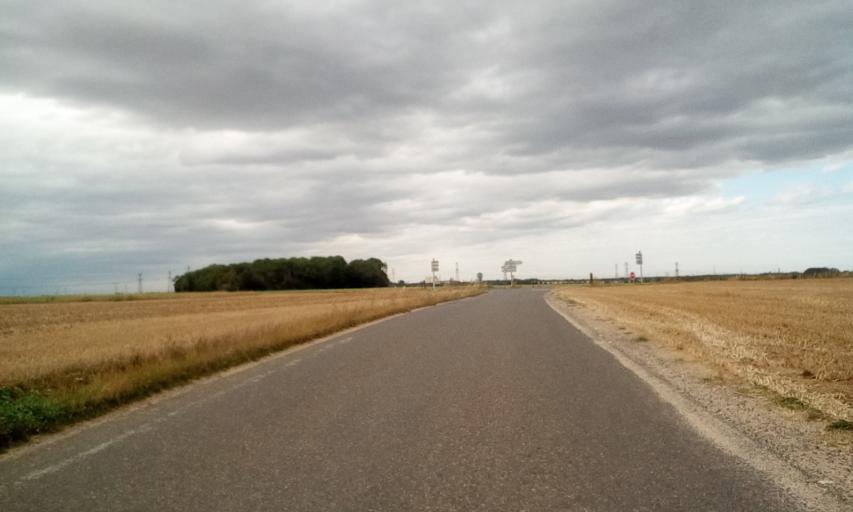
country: FR
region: Lower Normandy
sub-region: Departement du Calvados
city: Bellengreville
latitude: 49.1193
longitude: -0.2236
